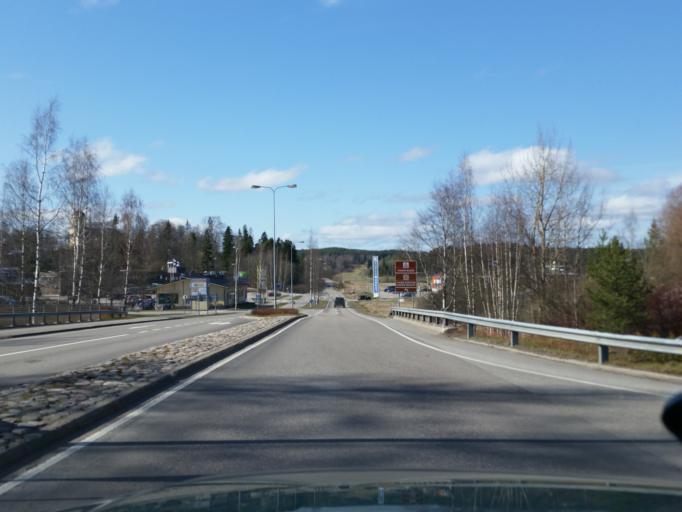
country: FI
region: Uusimaa
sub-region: Helsinki
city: Vihti
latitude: 60.4157
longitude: 24.3271
